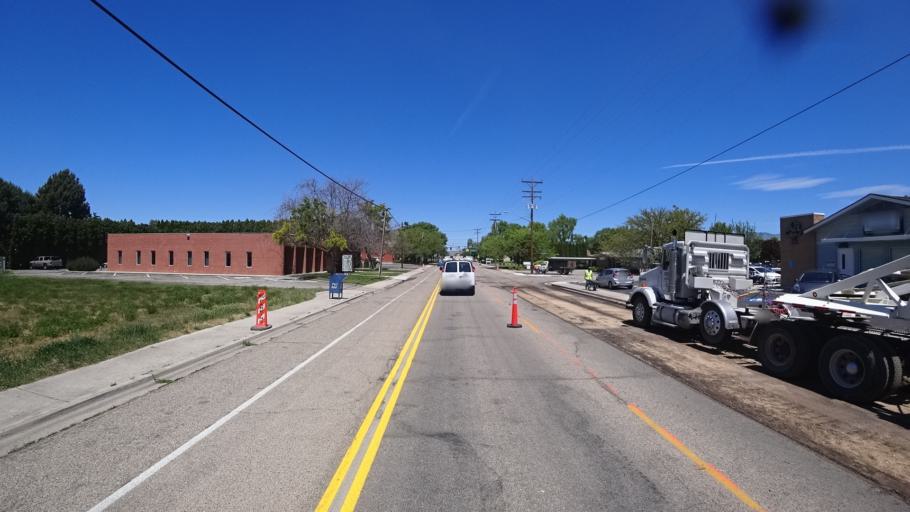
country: US
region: Idaho
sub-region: Ada County
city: Garden City
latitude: 43.5956
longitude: -116.2287
